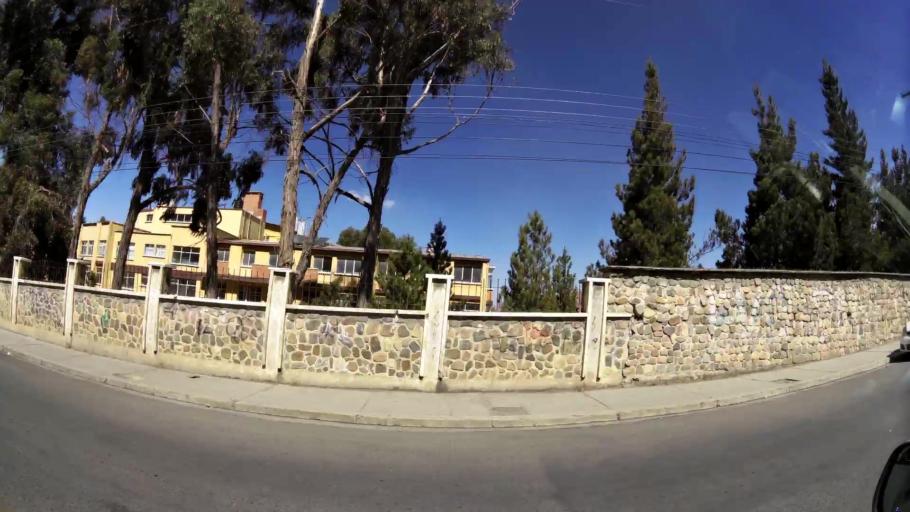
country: BO
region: La Paz
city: La Paz
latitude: -16.4871
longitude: -68.1582
